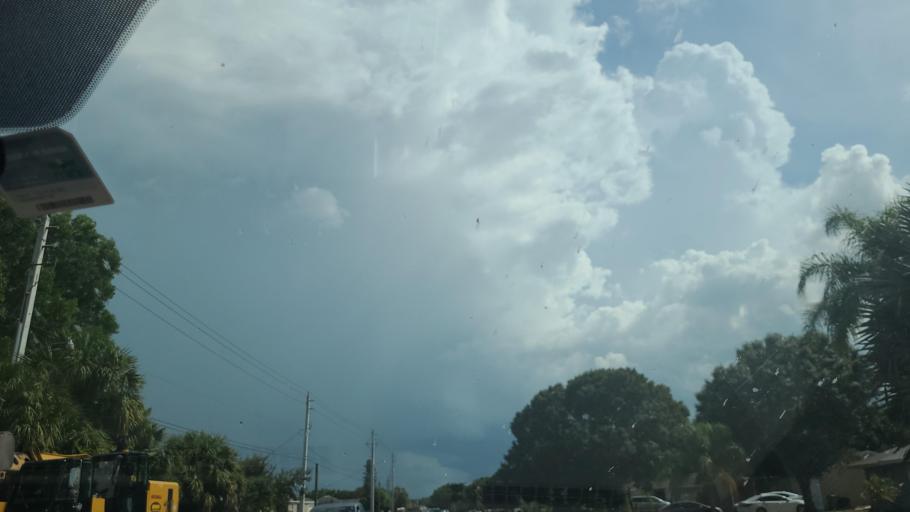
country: US
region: Florida
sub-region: Saint Lucie County
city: Port Saint Lucie
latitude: 27.2522
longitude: -80.3541
